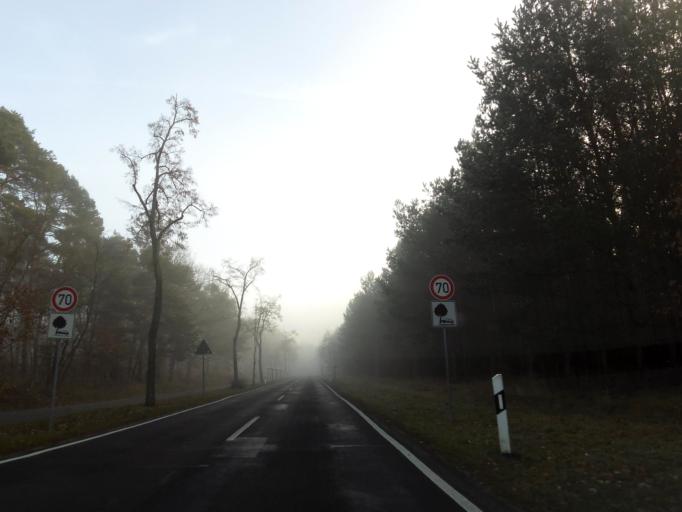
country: DE
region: Brandenburg
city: Werder
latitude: 52.3581
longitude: 12.9787
